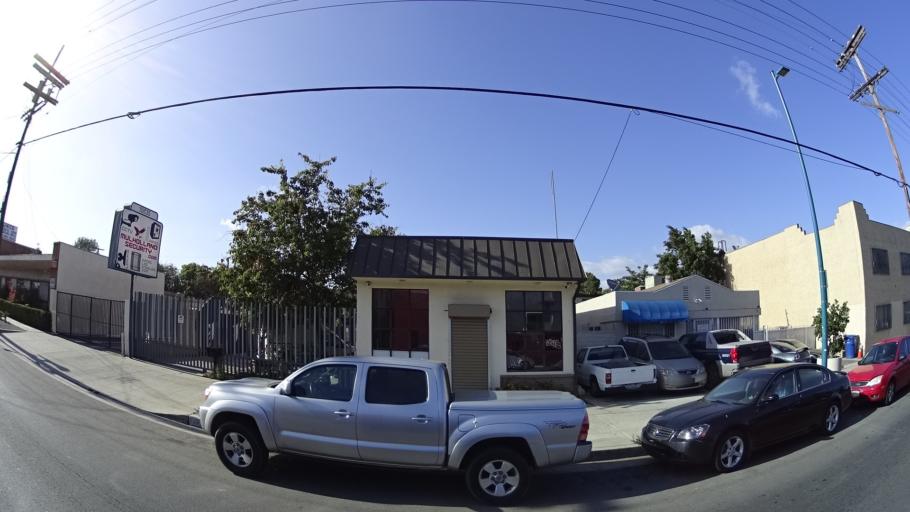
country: US
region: California
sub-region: Los Angeles County
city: North Hollywood
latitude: 34.1649
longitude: -118.3670
